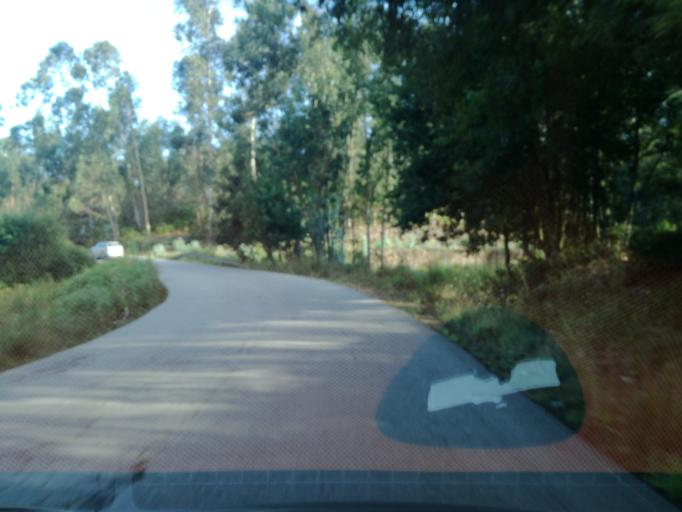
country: PT
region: Porto
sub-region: Valongo
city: Alfena
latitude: 41.2652
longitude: -8.5258
